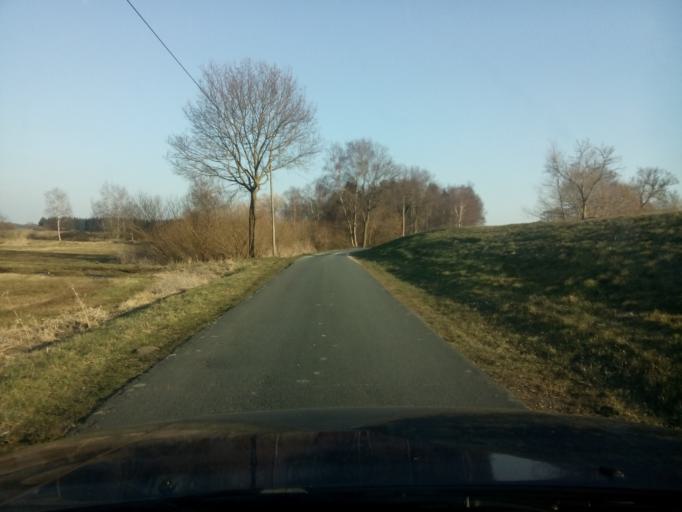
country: DE
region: Lower Saxony
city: Lilienthal
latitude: 53.1442
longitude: 8.8529
